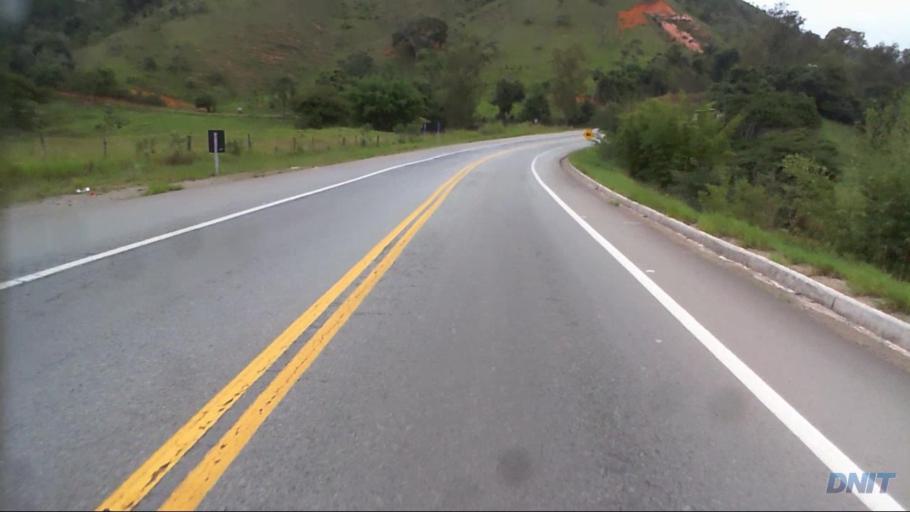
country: BR
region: Minas Gerais
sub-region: Nova Era
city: Nova Era
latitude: -19.6439
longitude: -42.9220
